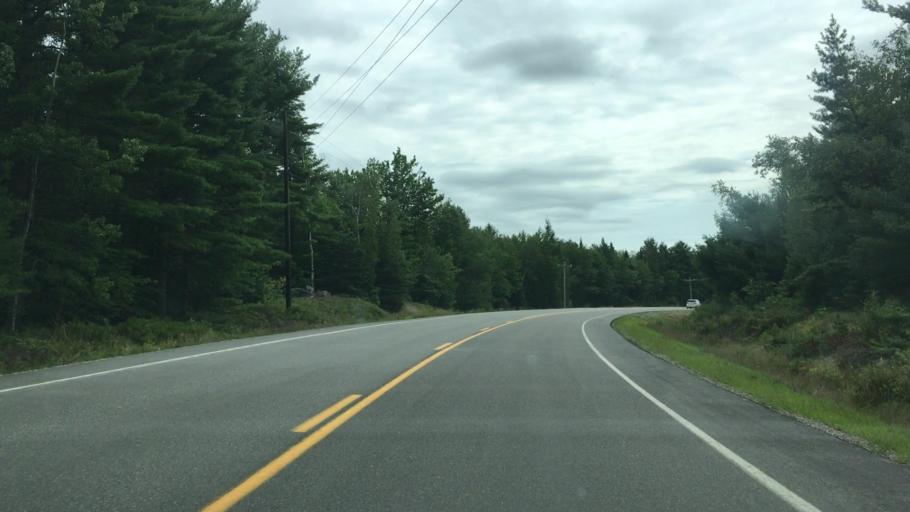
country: US
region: Maine
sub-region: Washington County
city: Machias
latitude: 45.0007
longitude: -67.5726
